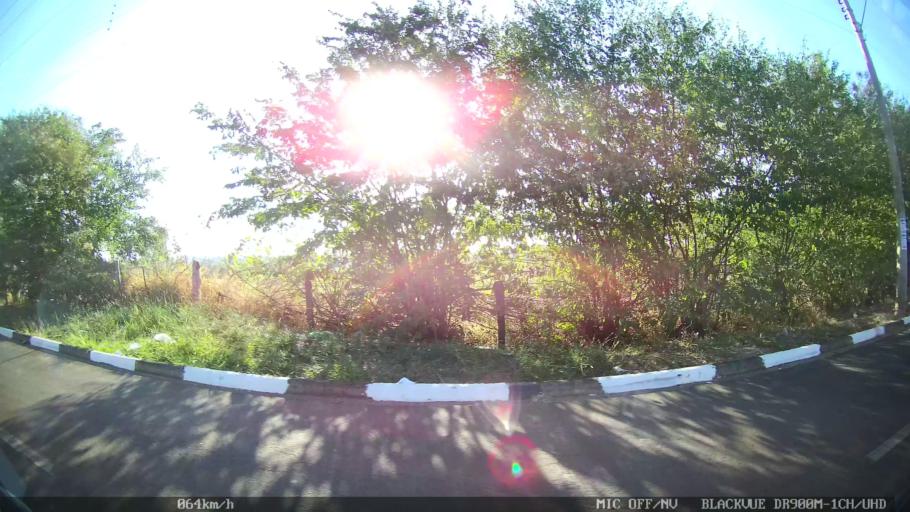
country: BR
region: Sao Paulo
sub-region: Franca
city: Franca
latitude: -20.5092
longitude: -47.3731
